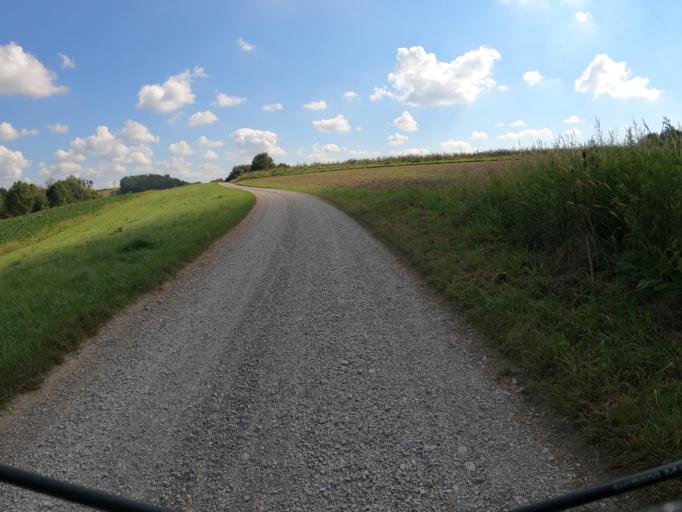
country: DE
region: Bavaria
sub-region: Swabia
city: Pfaffenhofen an der Roth
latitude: 48.3696
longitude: 10.1839
